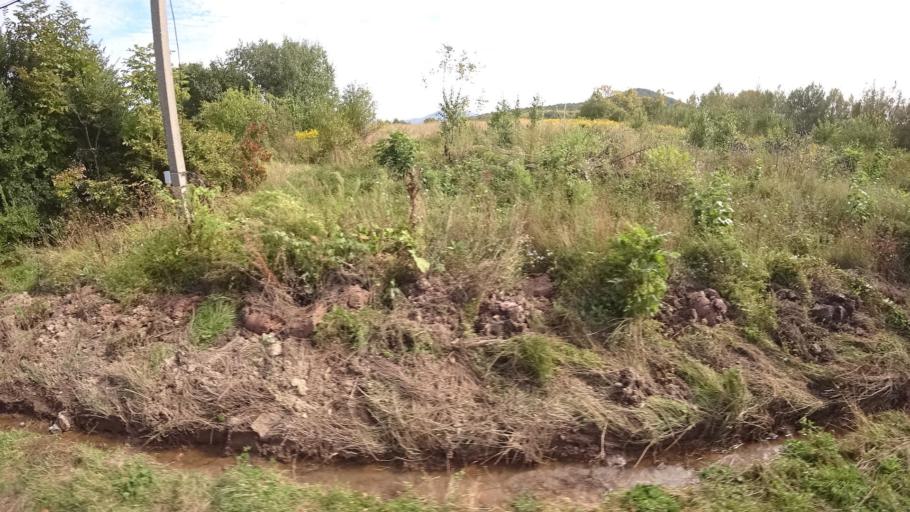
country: RU
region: Primorskiy
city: Yakovlevka
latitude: 44.3938
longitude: 133.6036
